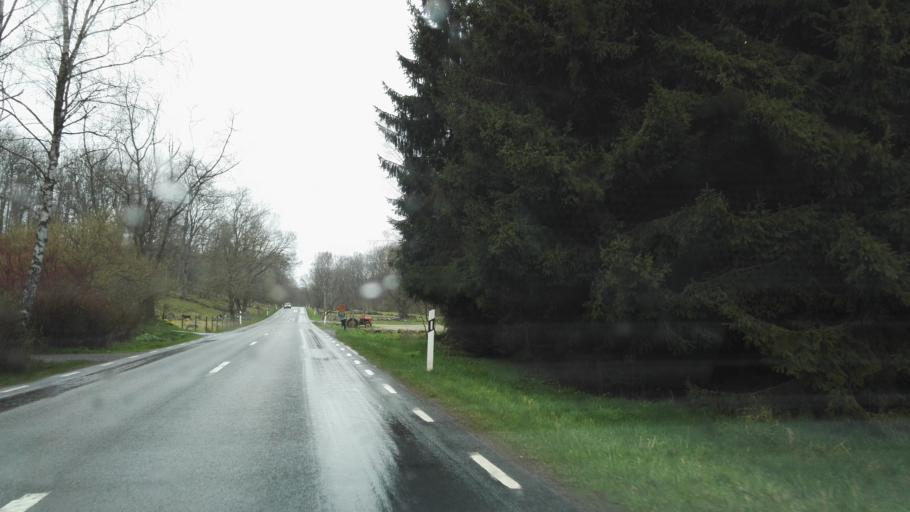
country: SE
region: Skane
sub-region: Simrishamns Kommun
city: Kivik
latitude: 55.6510
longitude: 14.2192
